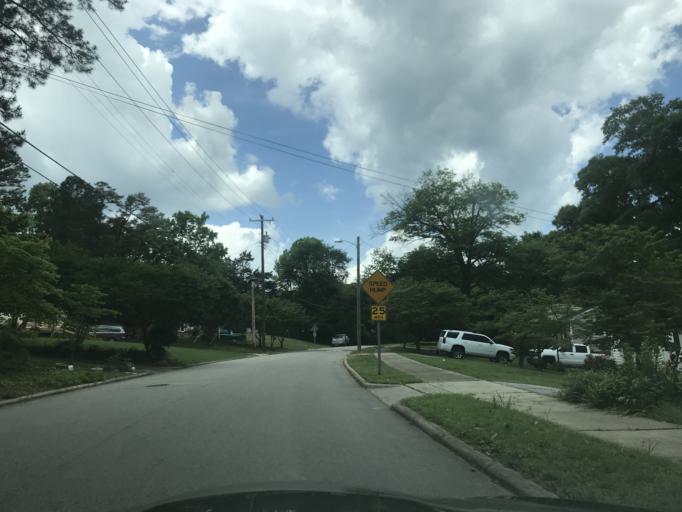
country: US
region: North Carolina
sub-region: Wake County
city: Raleigh
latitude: 35.8015
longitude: -78.6065
